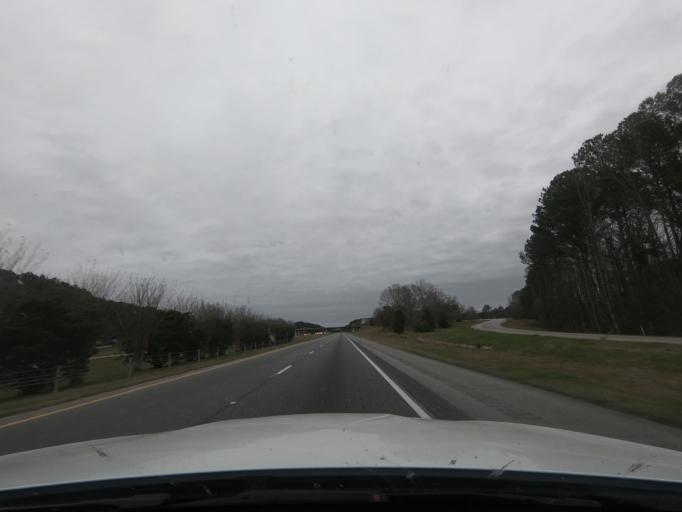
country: US
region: Georgia
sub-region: Harris County
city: Pine Mountain
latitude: 32.8545
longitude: -84.9825
